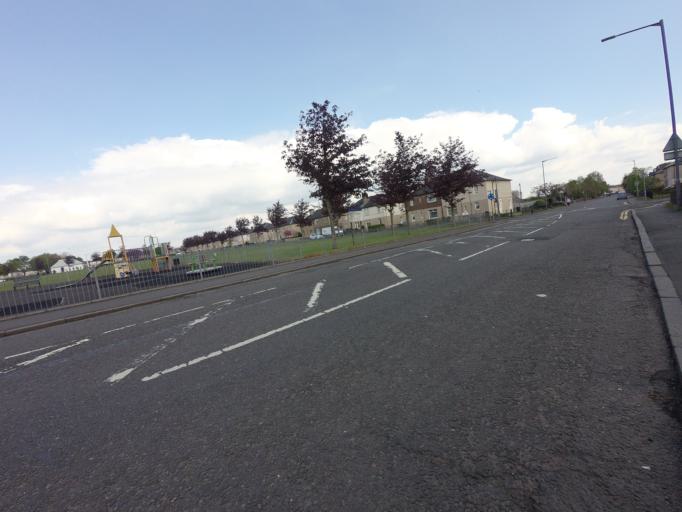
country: GB
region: Scotland
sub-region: Falkirk
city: Falkirk
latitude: 56.0154
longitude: -3.7859
